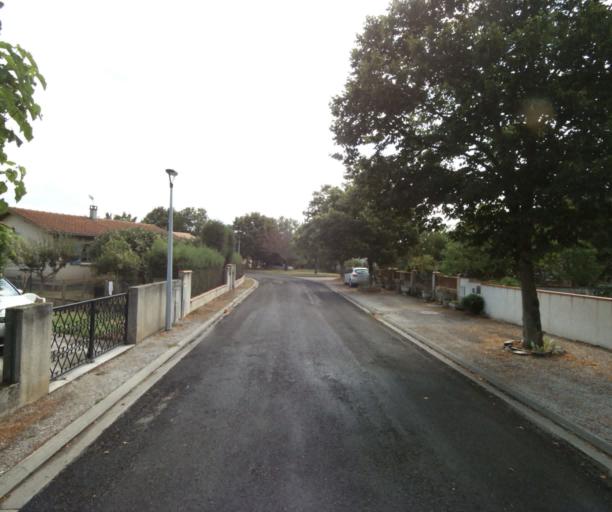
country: FR
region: Midi-Pyrenees
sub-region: Departement de la Haute-Garonne
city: Revel
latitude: 43.4602
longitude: 1.9928
